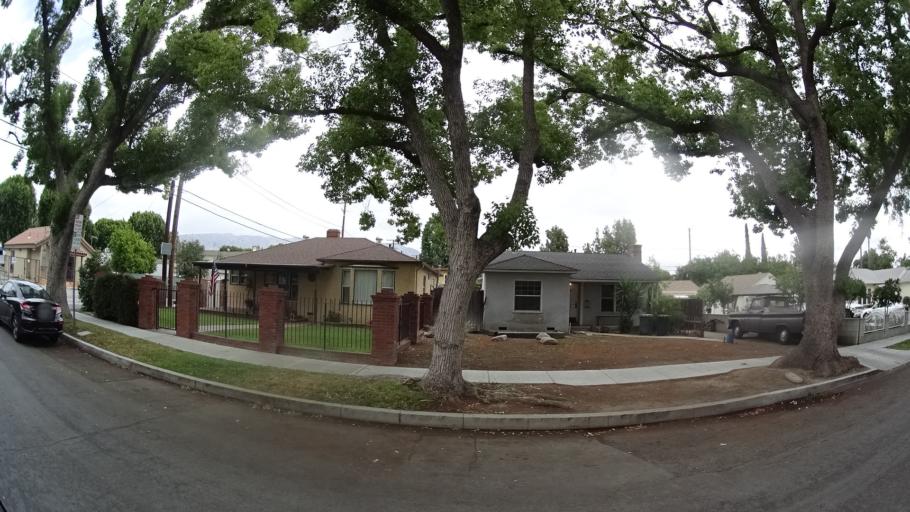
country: US
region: California
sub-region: Los Angeles County
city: Burbank
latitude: 34.1741
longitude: -118.3263
